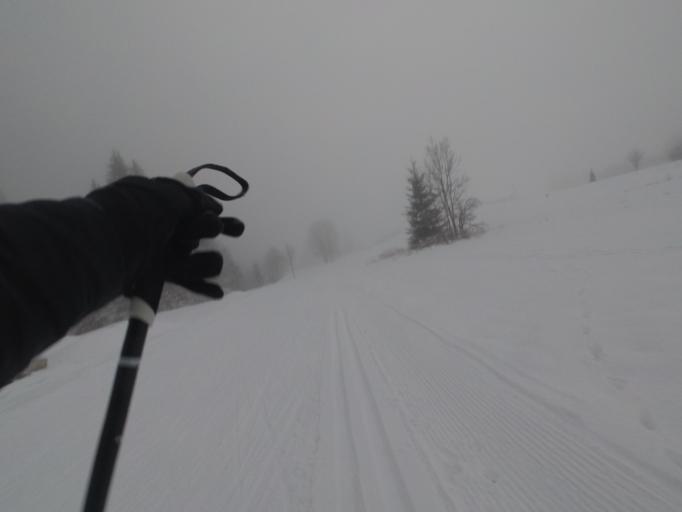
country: AT
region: Salzburg
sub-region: Politischer Bezirk Sankt Johann im Pongau
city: Wagrain
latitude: 47.3459
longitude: 13.3101
